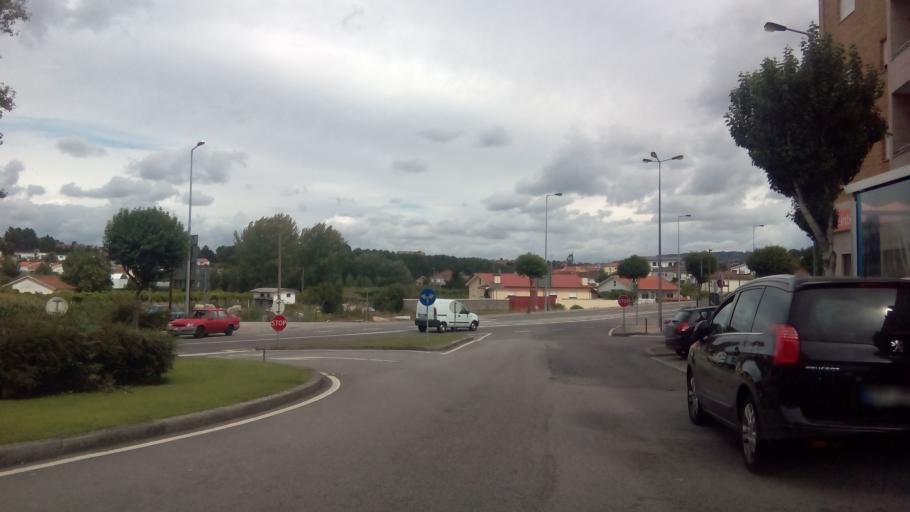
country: PT
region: Porto
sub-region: Paredes
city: Paredes
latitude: 41.2097
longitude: -8.3309
